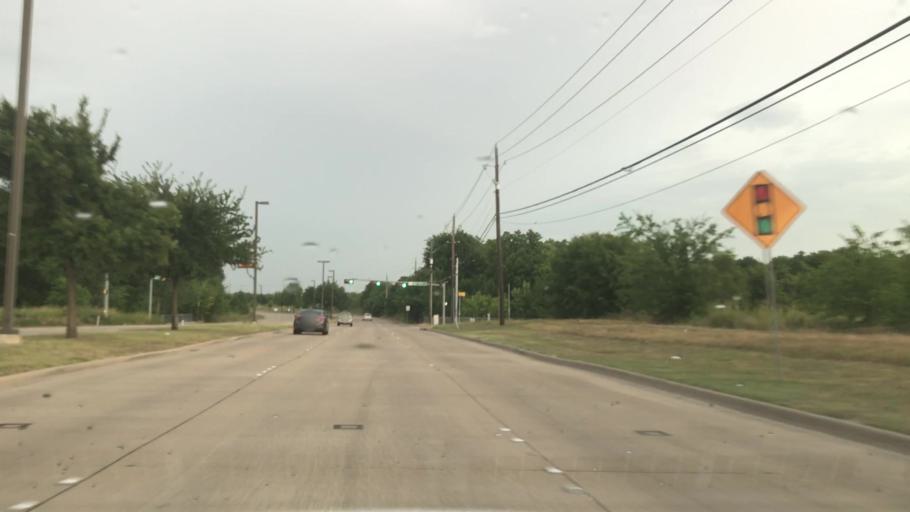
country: US
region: Texas
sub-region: Dallas County
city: Mesquite
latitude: 32.7392
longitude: -96.5737
